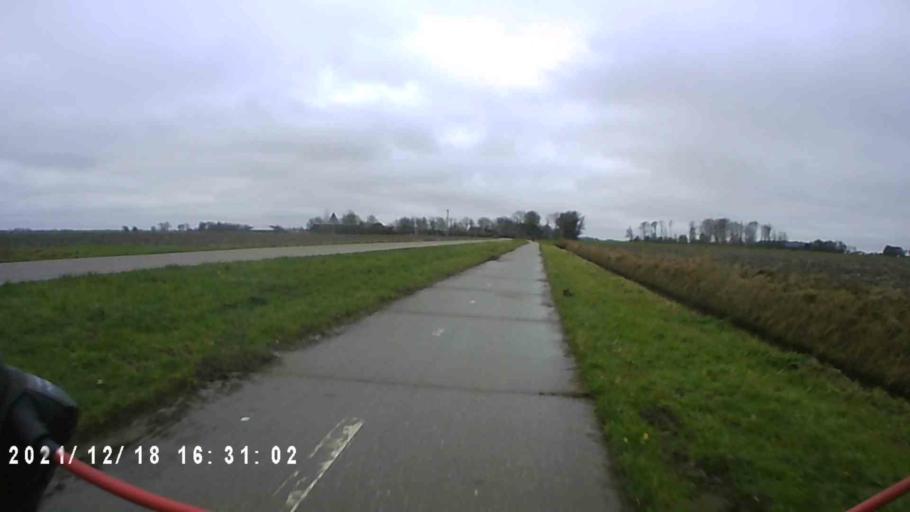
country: NL
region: Friesland
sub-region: Gemeente Dongeradeel
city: Dokkum
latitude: 53.3584
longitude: 6.0396
